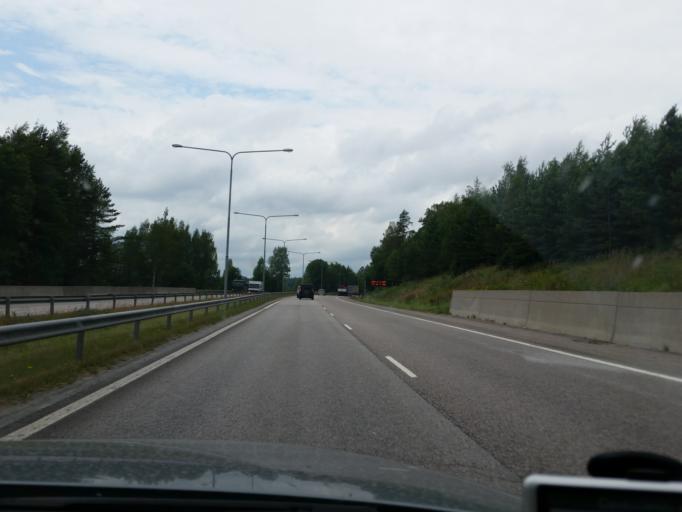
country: FI
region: Uusimaa
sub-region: Helsinki
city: Espoo
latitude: 60.2238
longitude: 24.6201
